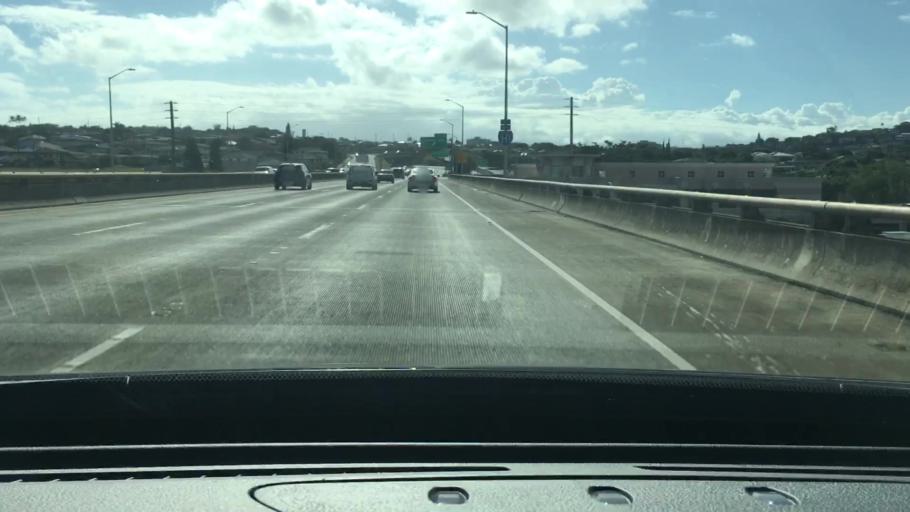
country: US
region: Hawaii
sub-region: Honolulu County
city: Honolulu
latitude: 21.2787
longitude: -157.7869
